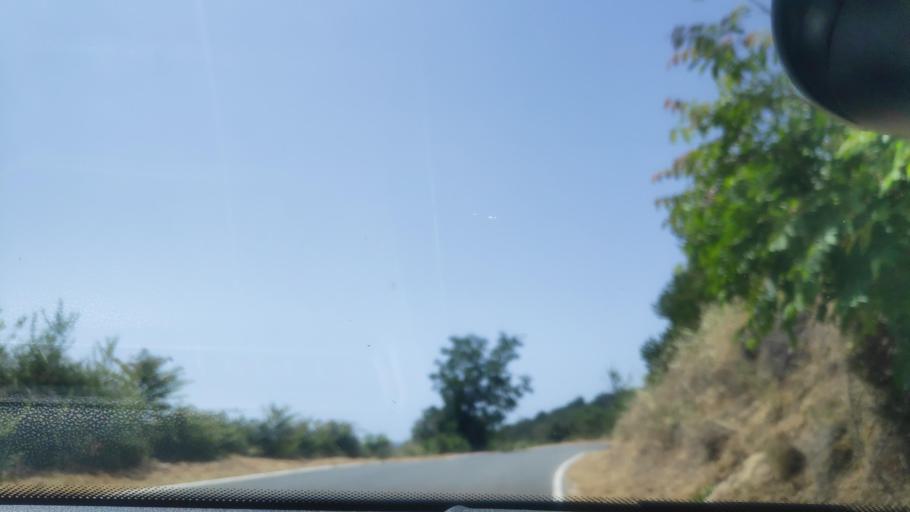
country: ES
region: Andalusia
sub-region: Provincia de Granada
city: Trevelez
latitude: 36.9732
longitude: -3.2785
